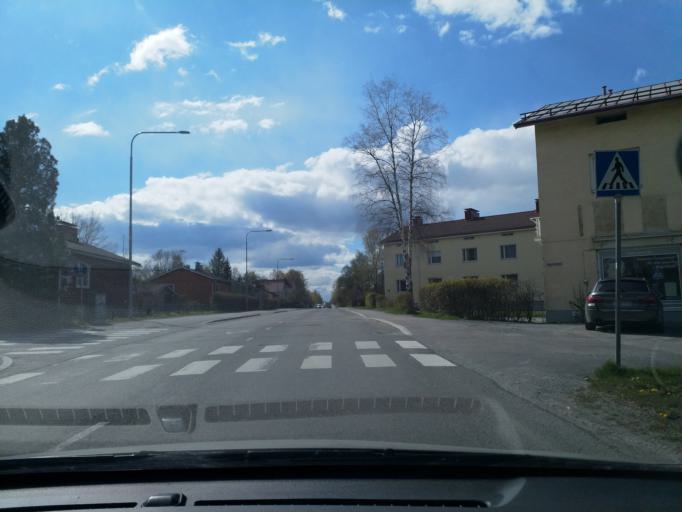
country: FI
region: Pirkanmaa
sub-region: Tampere
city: Tampere
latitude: 61.4828
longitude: 23.8023
